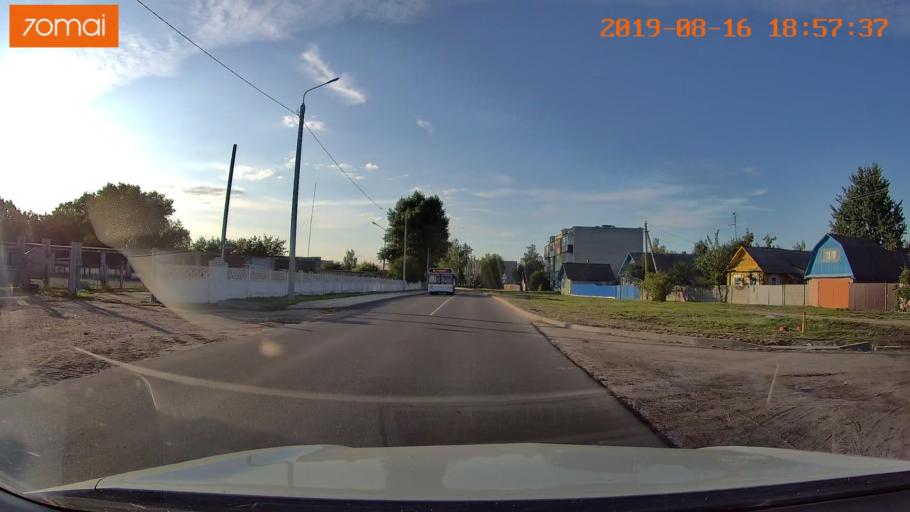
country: BY
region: Mogilev
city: Asipovichy
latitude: 53.2911
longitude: 28.6498
